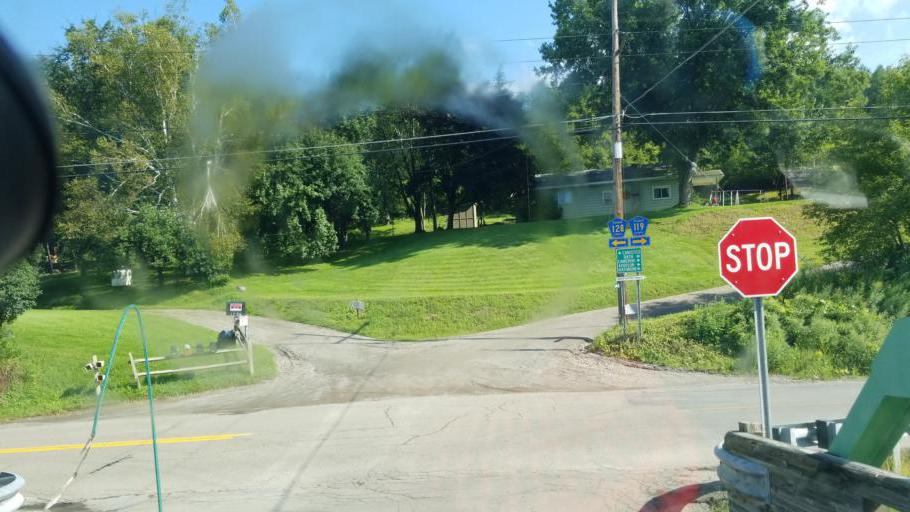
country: US
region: New York
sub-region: Steuben County
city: Canisteo
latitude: 42.2651
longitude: -77.5772
